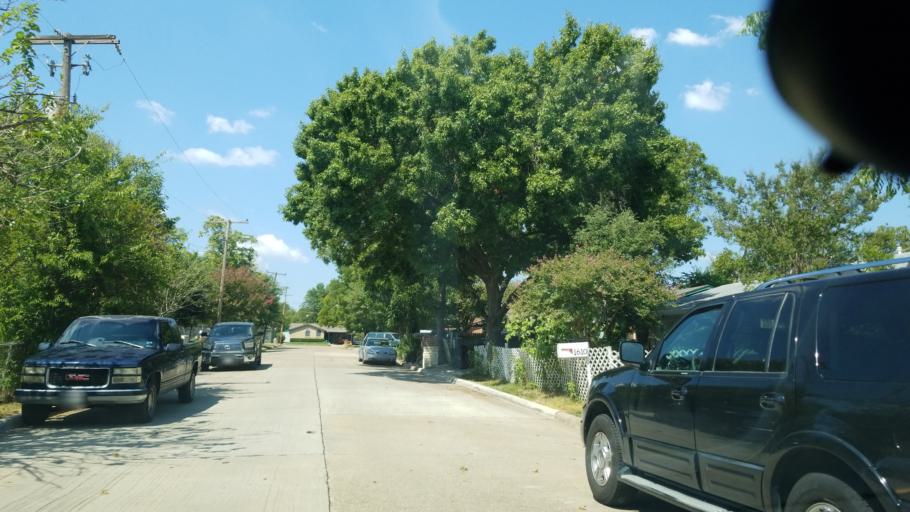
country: US
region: Texas
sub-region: Dallas County
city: Grand Prairie
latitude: 32.7098
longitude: -96.9831
